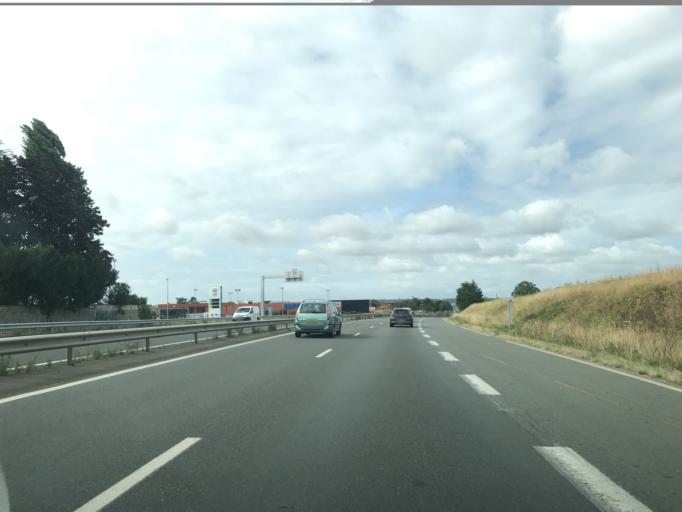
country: FR
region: Poitou-Charentes
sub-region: Departement de la Vienne
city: Vivonne
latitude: 46.4334
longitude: 0.2635
